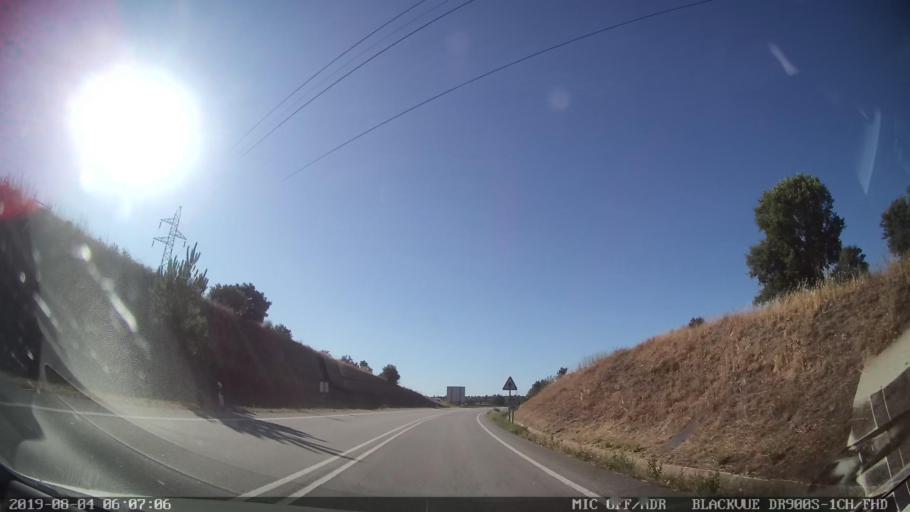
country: PT
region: Santarem
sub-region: Abrantes
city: Alferrarede
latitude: 39.4875
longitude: -8.0978
